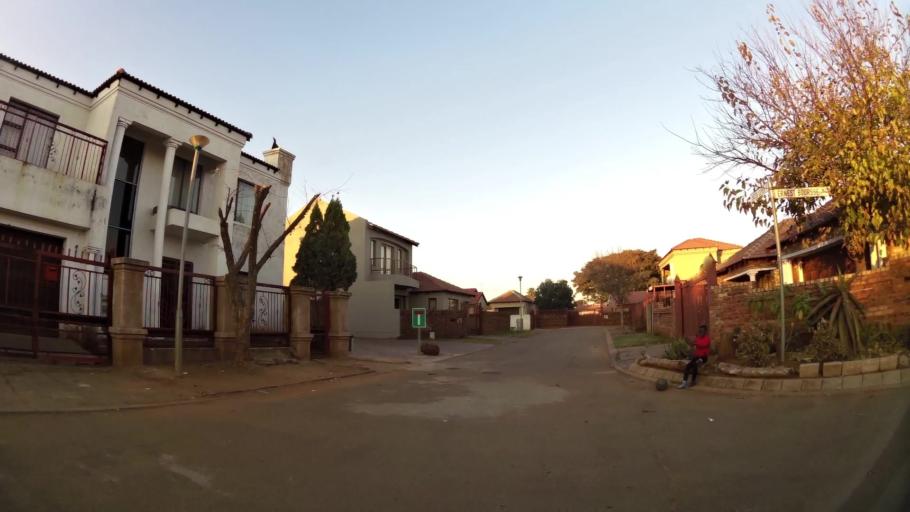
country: ZA
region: Gauteng
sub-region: City of Tshwane Metropolitan Municipality
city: Pretoria
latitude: -25.7419
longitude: 28.1383
